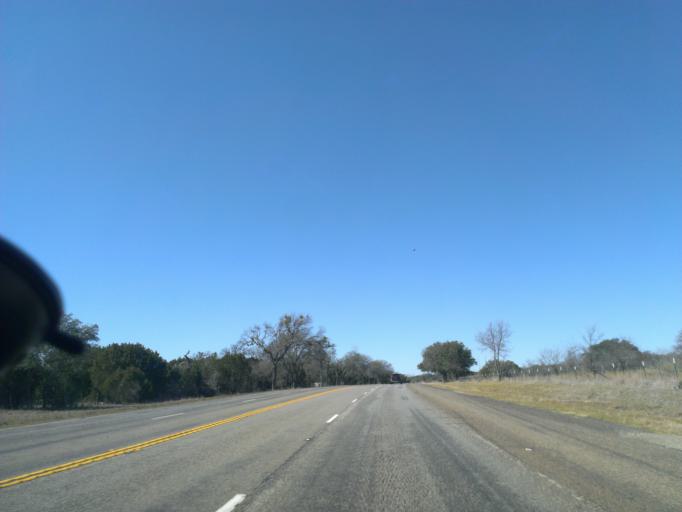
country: US
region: Texas
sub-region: Lampasas County
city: Kempner
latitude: 30.9281
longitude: -98.0000
